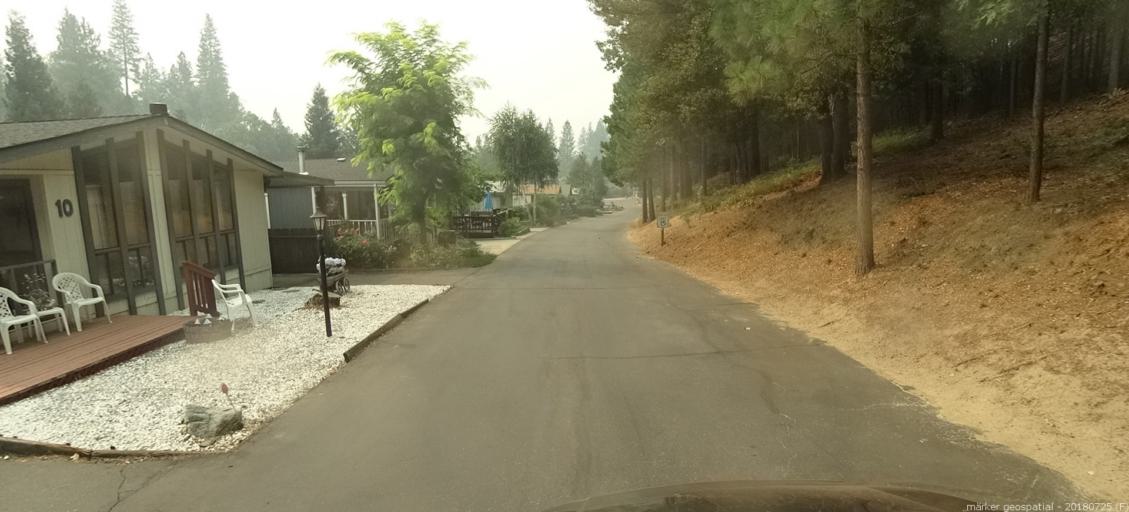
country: US
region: California
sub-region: Madera County
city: Oakhurst
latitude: 37.3262
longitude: -119.5532
